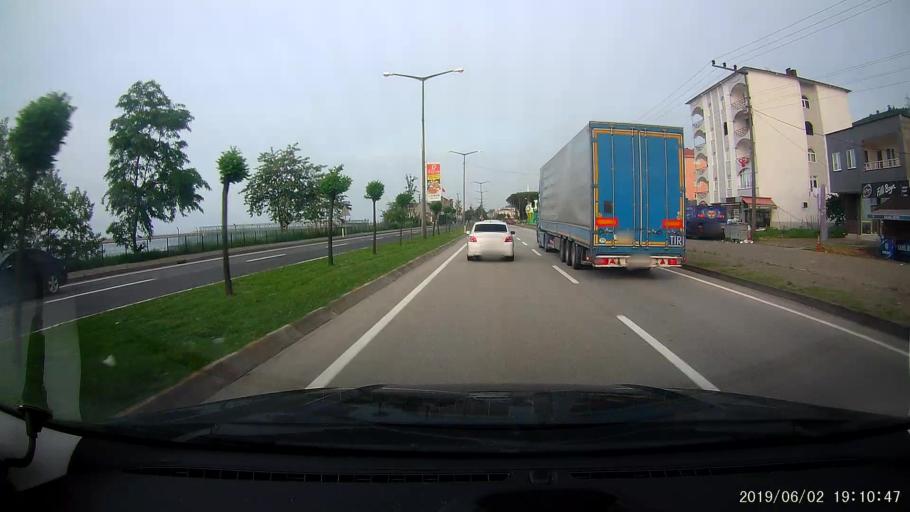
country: TR
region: Ordu
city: Gulyali
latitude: 40.9678
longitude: 38.0514
